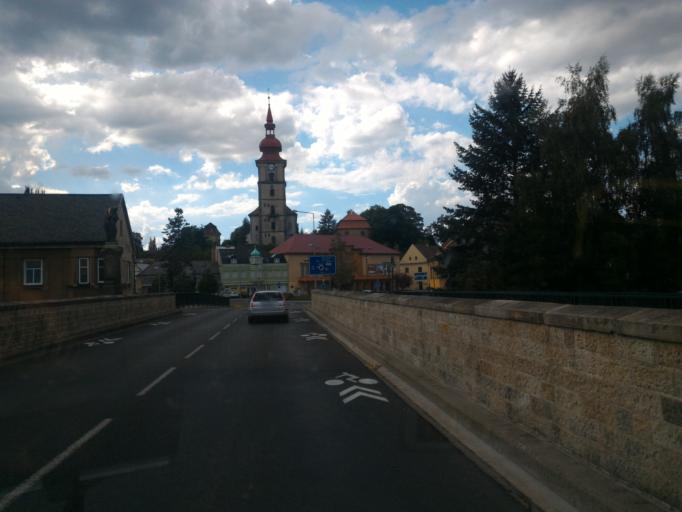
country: CZ
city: Mimon
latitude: 50.6546
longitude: 14.7272
